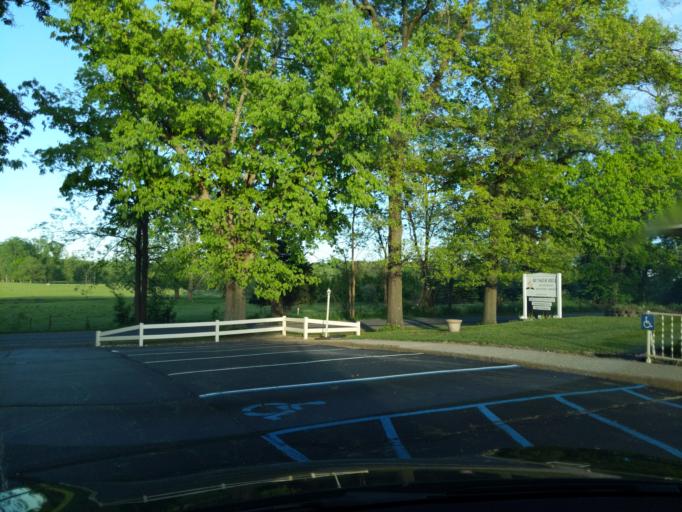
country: US
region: Michigan
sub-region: Ingham County
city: Leslie
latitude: 42.4730
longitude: -84.3174
